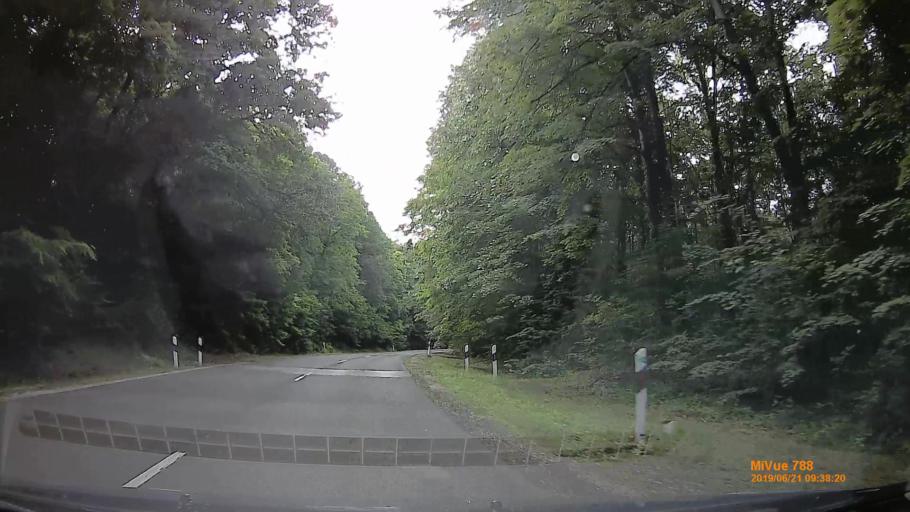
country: HU
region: Somogy
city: Taszar
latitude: 46.3084
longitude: 17.9231
